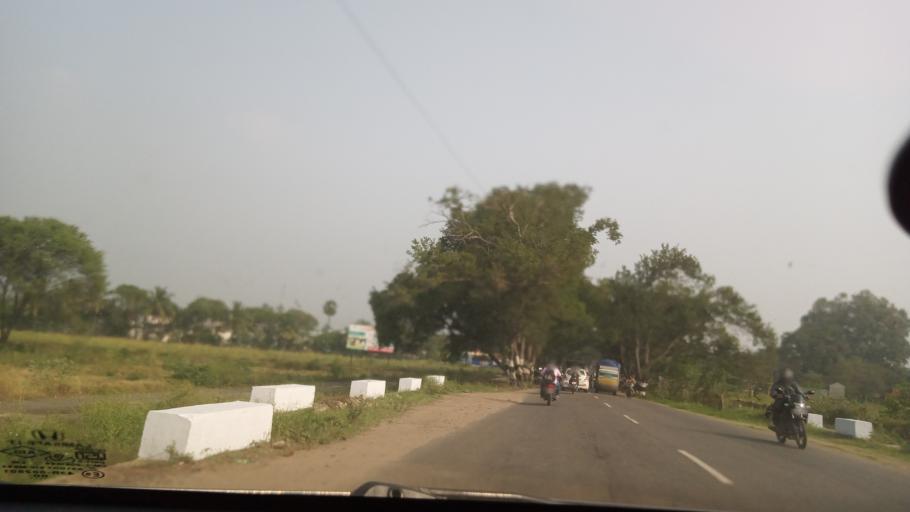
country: IN
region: Tamil Nadu
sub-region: Coimbatore
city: Periyanayakkanpalaiyam
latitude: 11.1545
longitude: 77.0498
